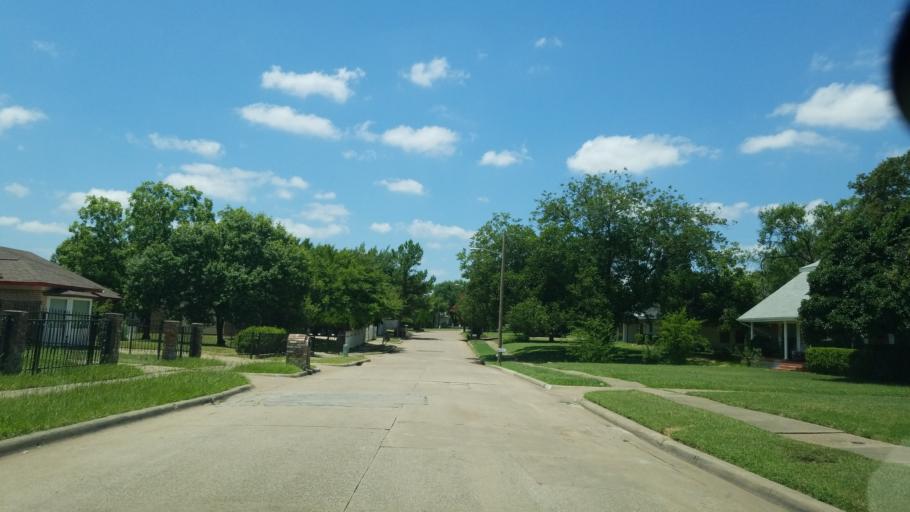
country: US
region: Texas
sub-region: Dallas County
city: Balch Springs
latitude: 32.7430
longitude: -96.7026
